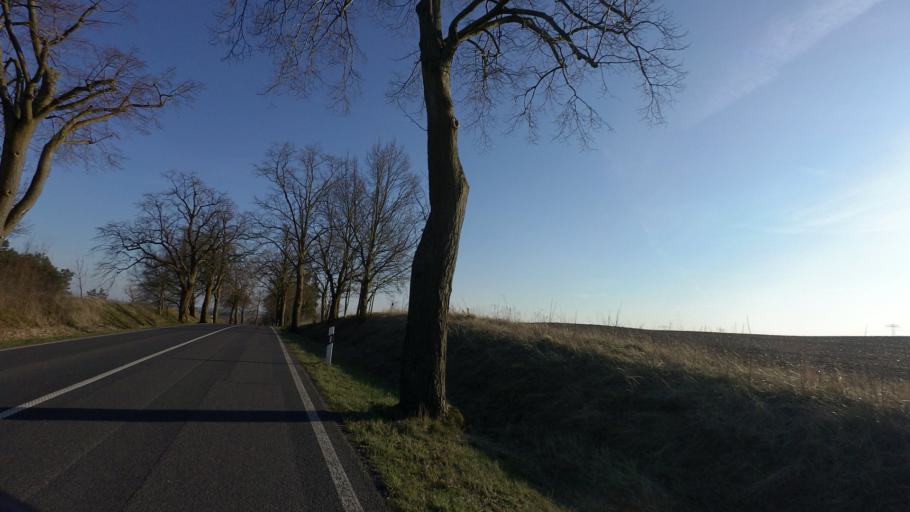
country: DE
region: Brandenburg
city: Britz
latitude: 52.9016
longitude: 13.8027
